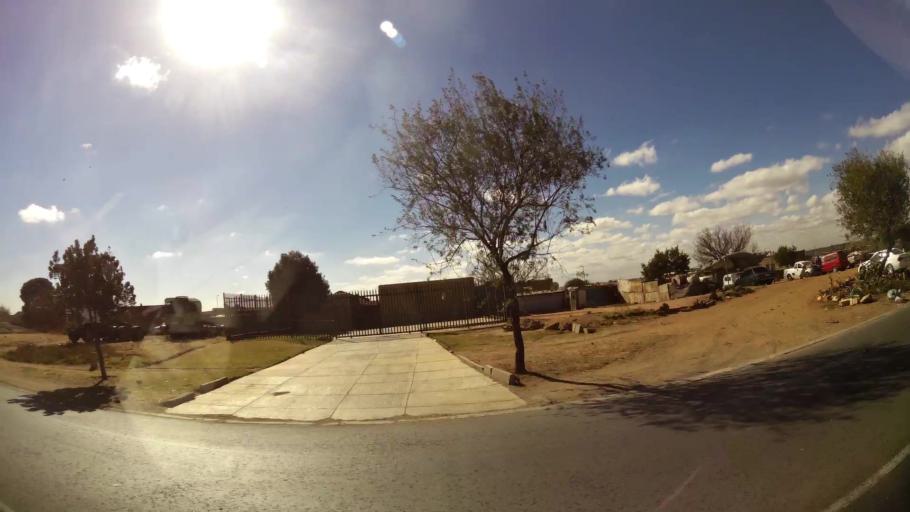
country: ZA
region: Gauteng
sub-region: City of Johannesburg Metropolitan Municipality
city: Modderfontein
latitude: -26.0517
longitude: 28.1764
